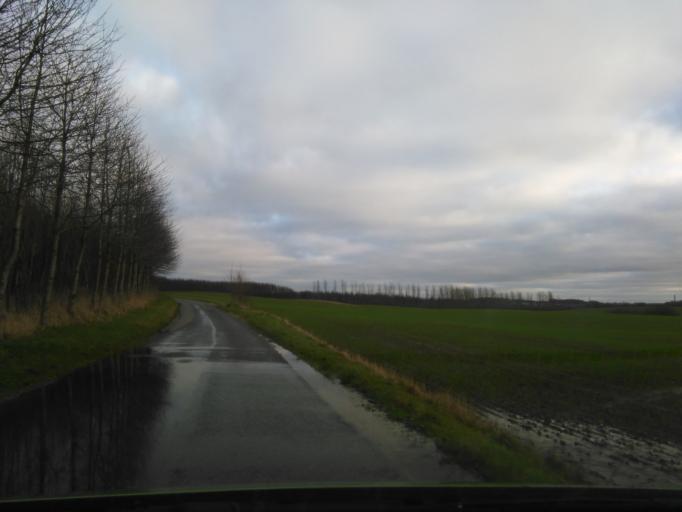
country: DK
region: Central Jutland
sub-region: Arhus Kommune
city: Sabro
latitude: 56.1690
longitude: 10.0665
